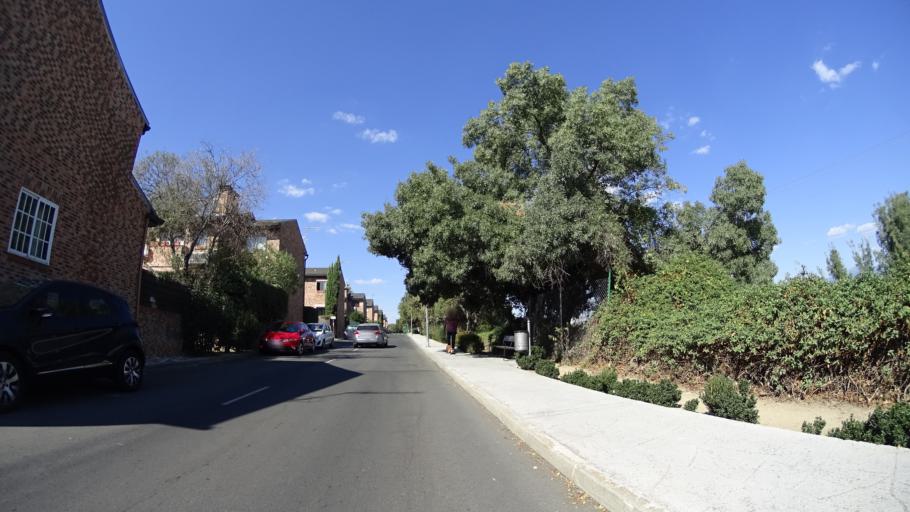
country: ES
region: Madrid
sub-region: Provincia de Madrid
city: Navalquejigo
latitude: 40.6087
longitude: -4.0269
